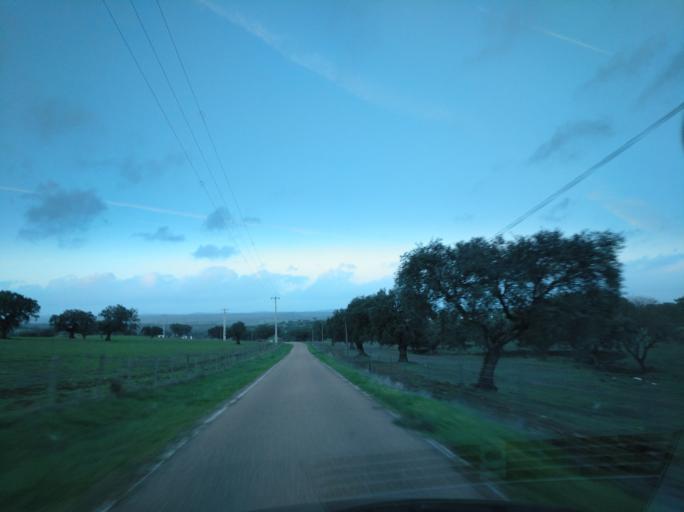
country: PT
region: Portalegre
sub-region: Campo Maior
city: Campo Maior
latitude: 39.0727
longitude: -7.1154
